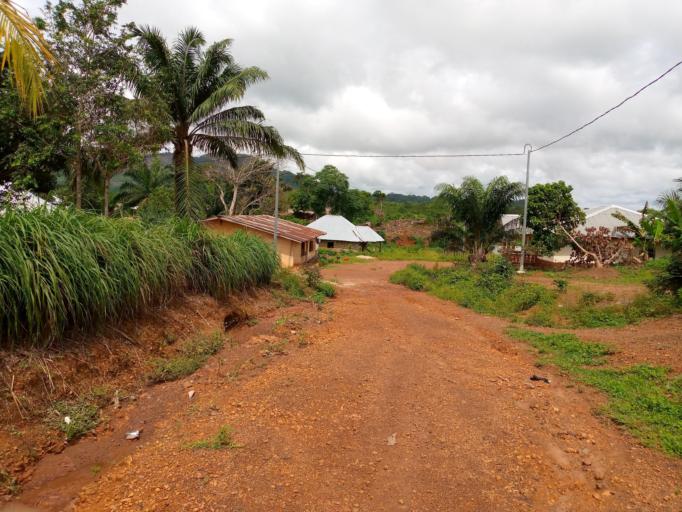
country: SL
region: Southern Province
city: Mogbwemo
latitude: 7.7581
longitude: -12.3099
